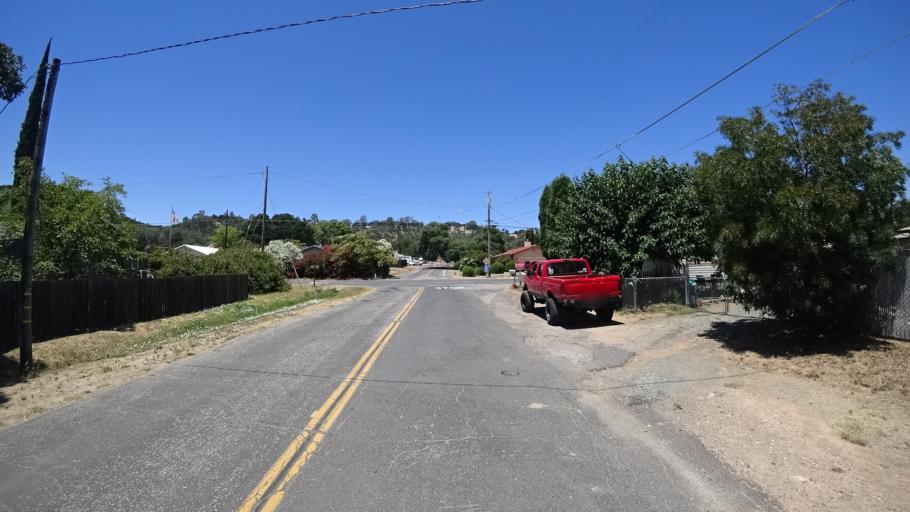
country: US
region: California
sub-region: Calaveras County
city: Valley Springs
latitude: 38.1914
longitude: -120.8313
